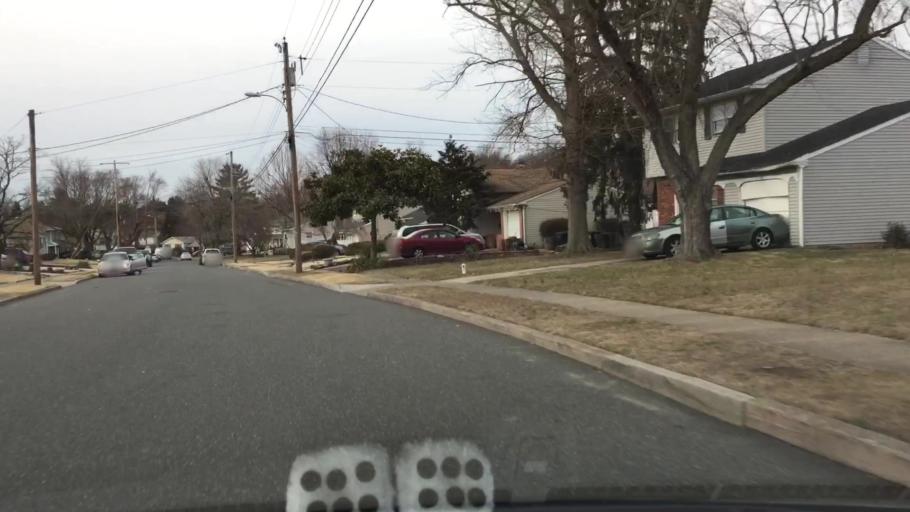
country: US
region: New Jersey
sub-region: Gloucester County
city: Turnersville
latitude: 39.7683
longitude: -75.0555
